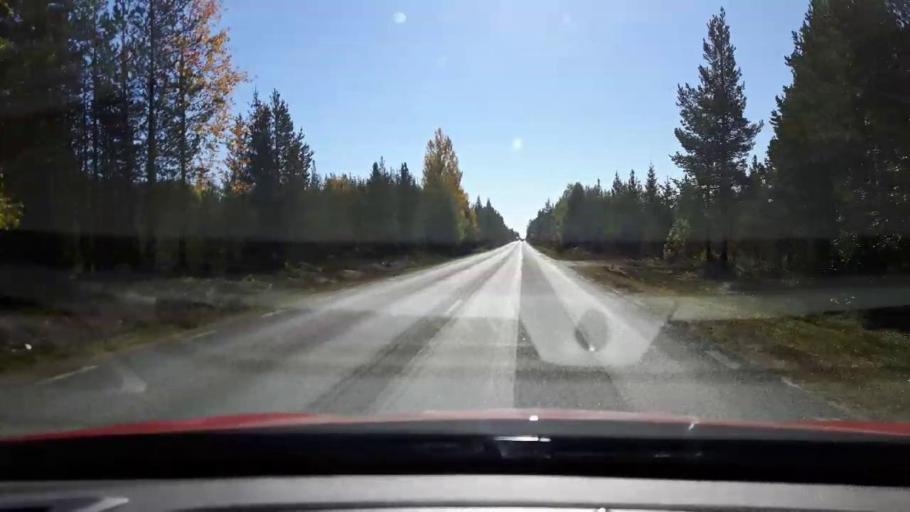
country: SE
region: Jaemtland
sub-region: Harjedalens Kommun
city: Sveg
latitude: 62.4178
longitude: 13.9115
